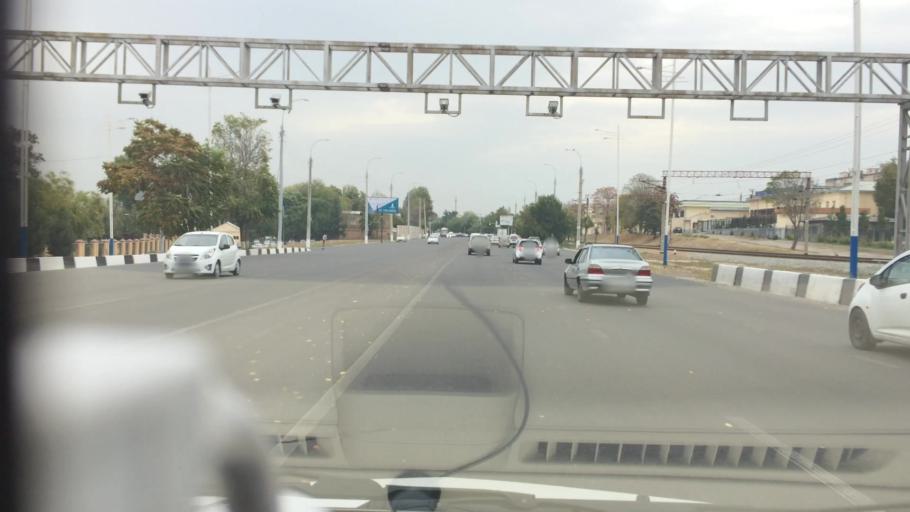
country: UZ
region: Toshkent Shahri
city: Tashkent
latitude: 41.3075
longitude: 69.3019
